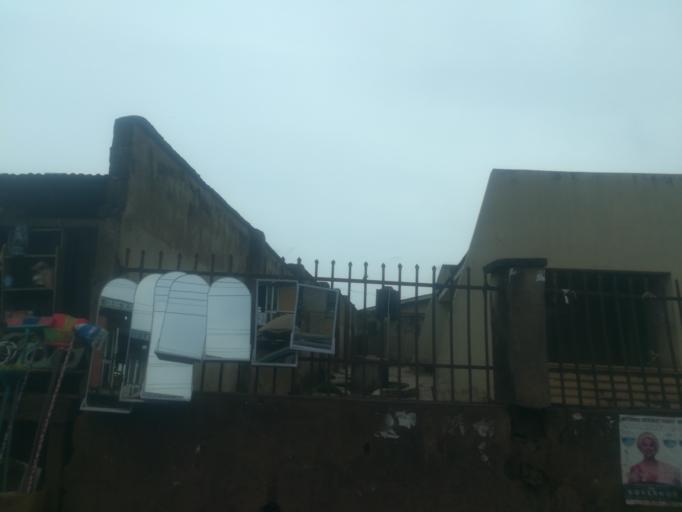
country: NG
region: Oyo
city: Ibadan
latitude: 7.3807
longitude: 3.9343
